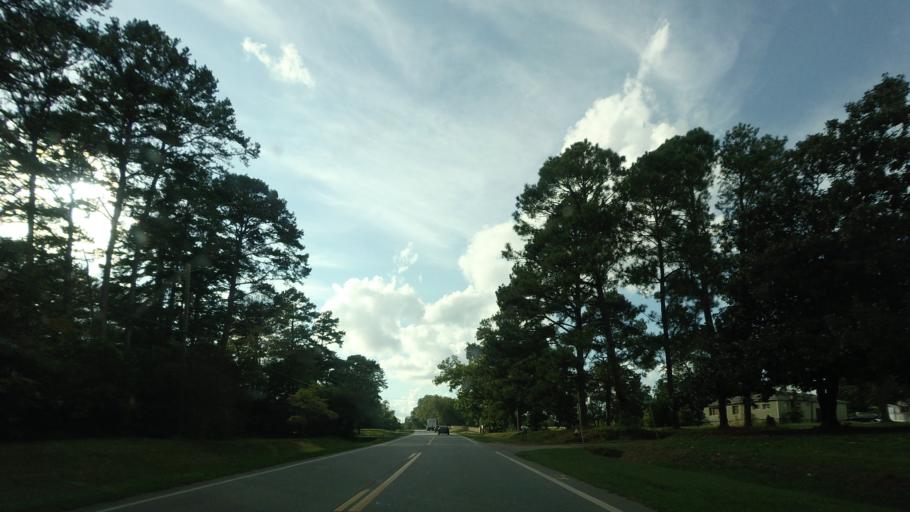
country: US
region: Georgia
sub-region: Pulaski County
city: Hawkinsville
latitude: 32.2866
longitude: -83.4853
